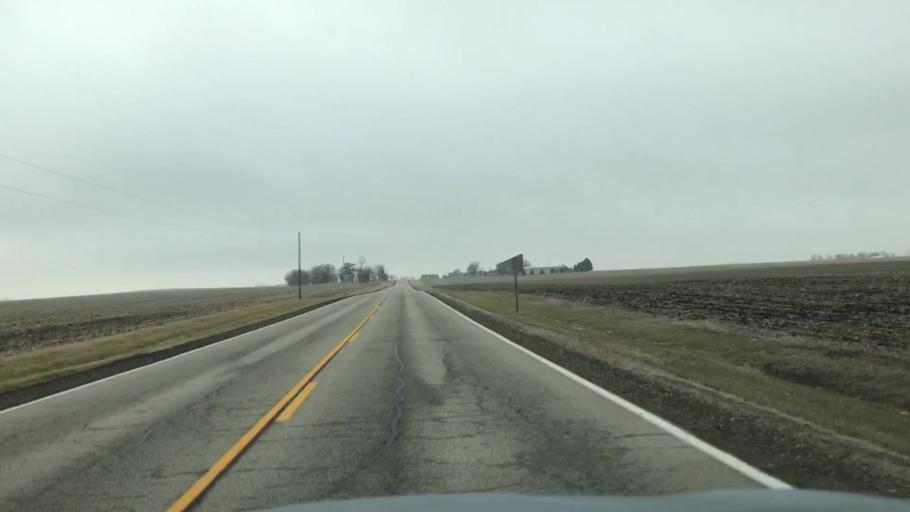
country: US
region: Illinois
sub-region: McLean County
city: Hudson
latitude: 40.5981
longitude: -88.9449
